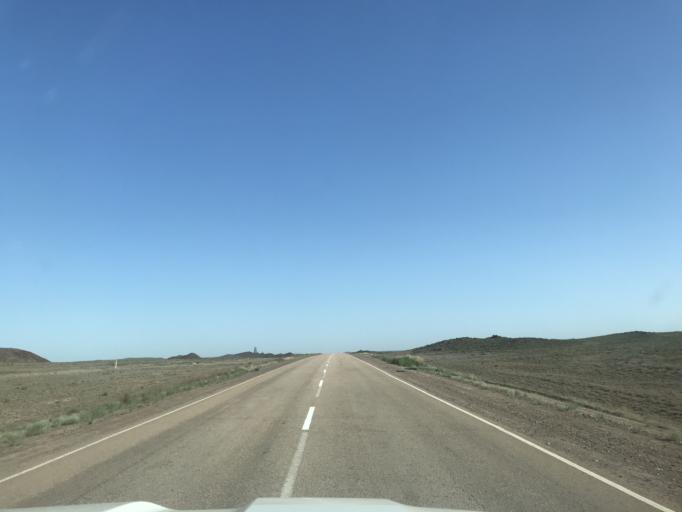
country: KZ
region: Zhambyl
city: Mynaral
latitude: 45.4250
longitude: 73.6208
